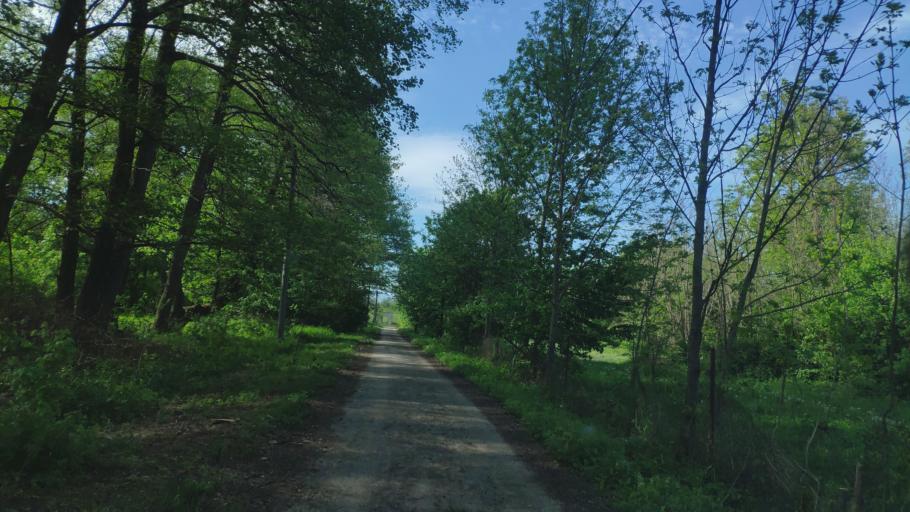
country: SK
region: Kosicky
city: Secovce
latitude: 48.7074
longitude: 21.6154
